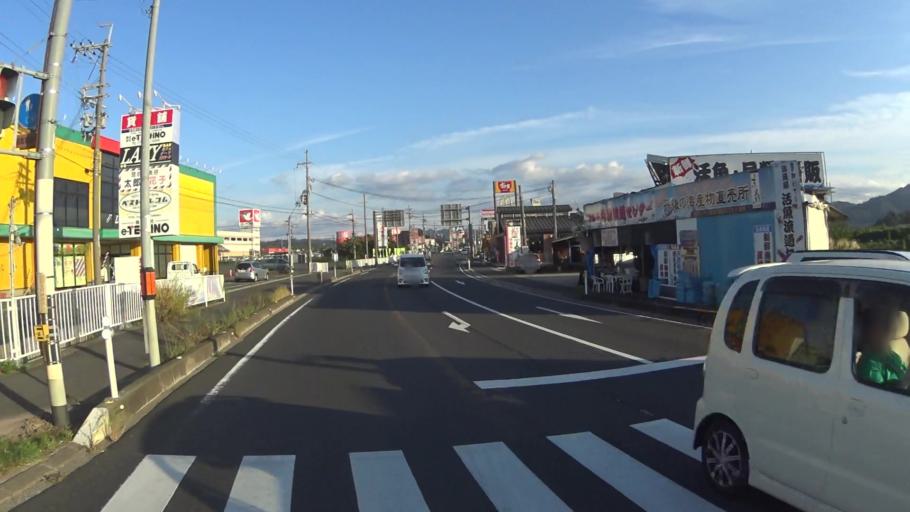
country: JP
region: Kyoto
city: Miyazu
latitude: 35.6096
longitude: 135.0795
